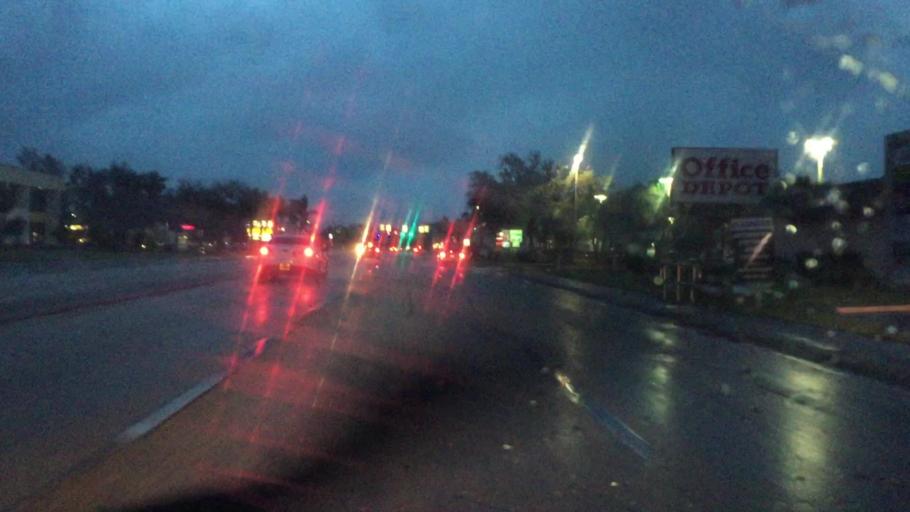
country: US
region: Florida
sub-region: Lee County
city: Villas
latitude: 26.5565
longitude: -81.8747
